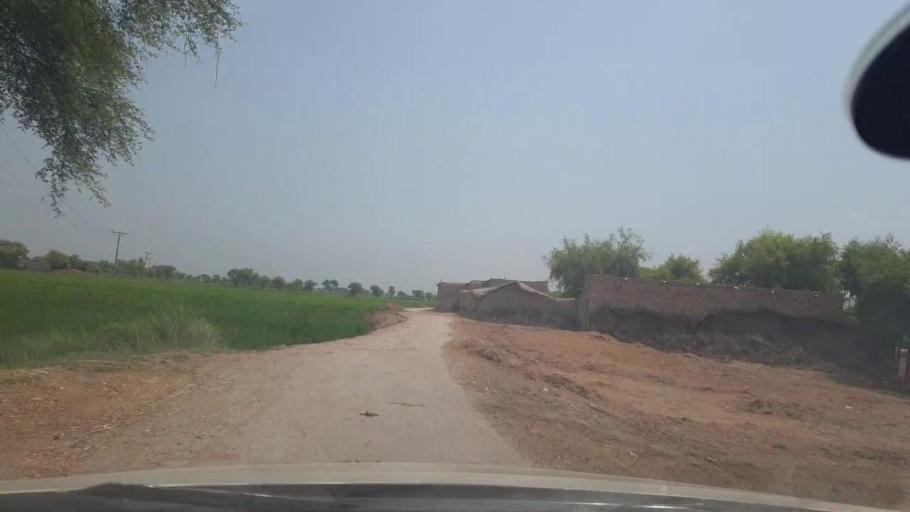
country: PK
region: Sindh
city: Jacobabad
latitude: 28.1753
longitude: 68.3857
